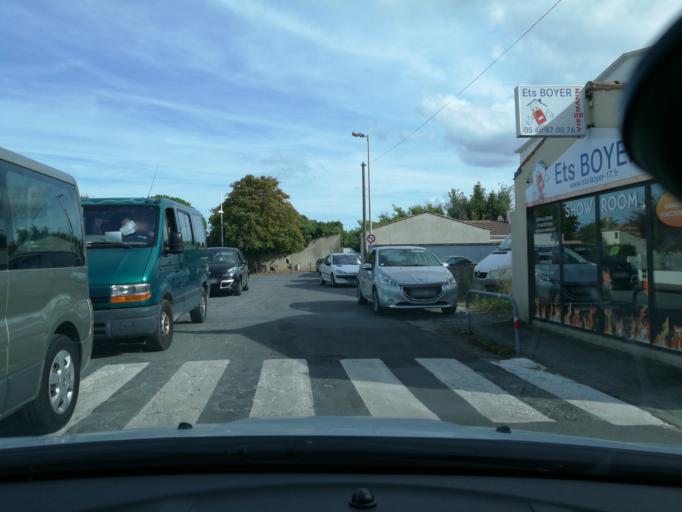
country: FR
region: Poitou-Charentes
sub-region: Departement de la Charente-Maritime
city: Dolus-d'Oleron
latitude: 45.9446
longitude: -1.3089
